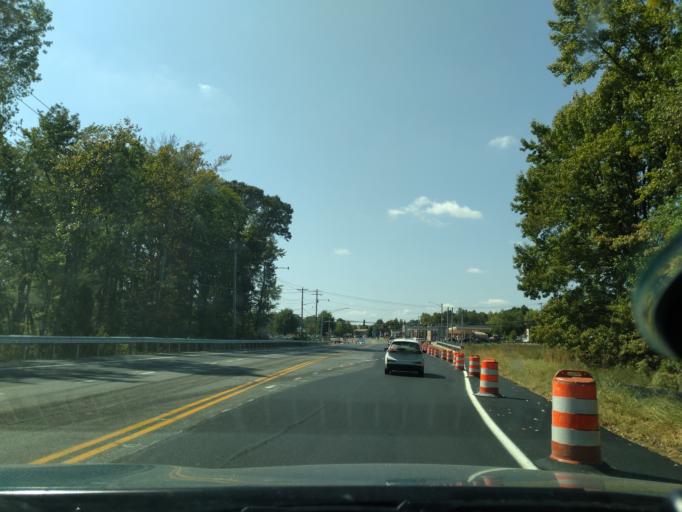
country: US
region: Maryland
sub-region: Calvert County
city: Prince Frederick
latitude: 38.5475
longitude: -76.5880
